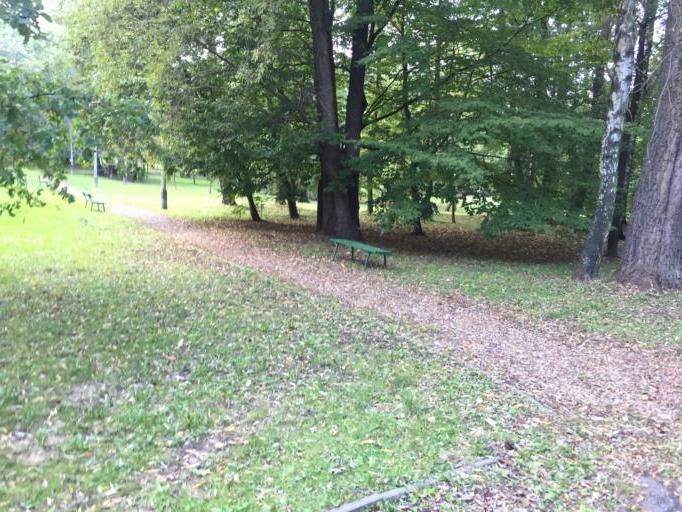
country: PL
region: Lesser Poland Voivodeship
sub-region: Powiat wielicki
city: Czarnochowice
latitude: 50.0193
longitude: 20.0023
